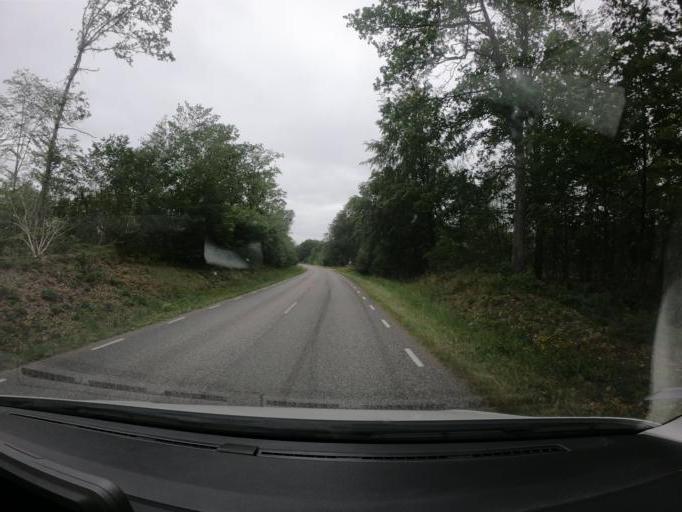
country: SE
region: Skane
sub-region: Perstorps Kommun
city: Perstorp
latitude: 56.1173
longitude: 13.4123
